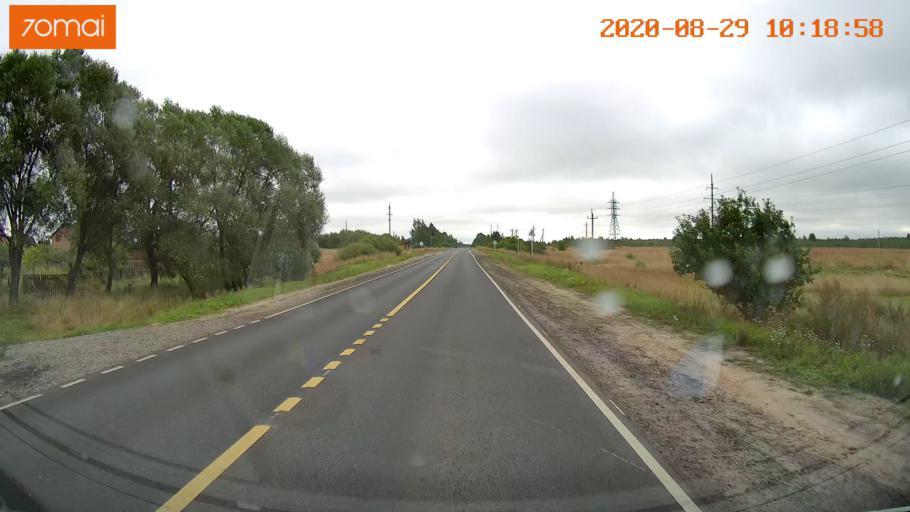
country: RU
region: Ivanovo
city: Yur'yevets
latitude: 57.3296
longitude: 42.8504
